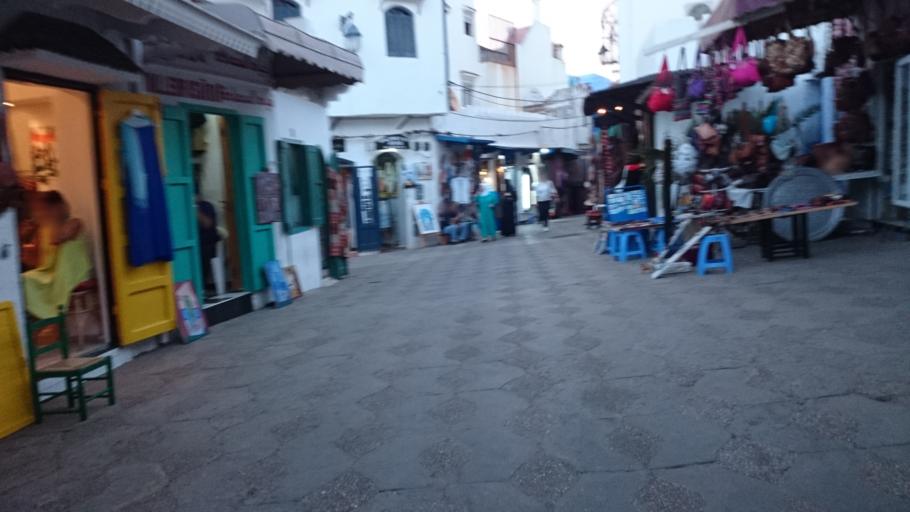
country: MA
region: Tanger-Tetouan
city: Asilah
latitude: 35.4658
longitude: -6.0385
